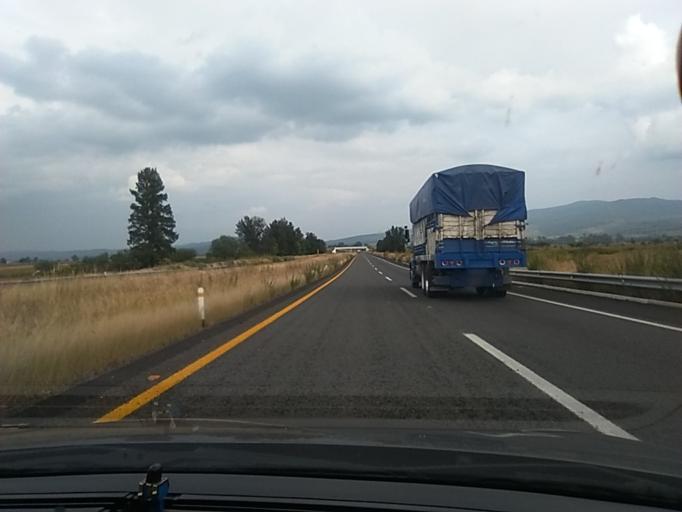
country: MX
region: Michoacan
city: Ecuandureo
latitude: 20.1758
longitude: -102.2397
